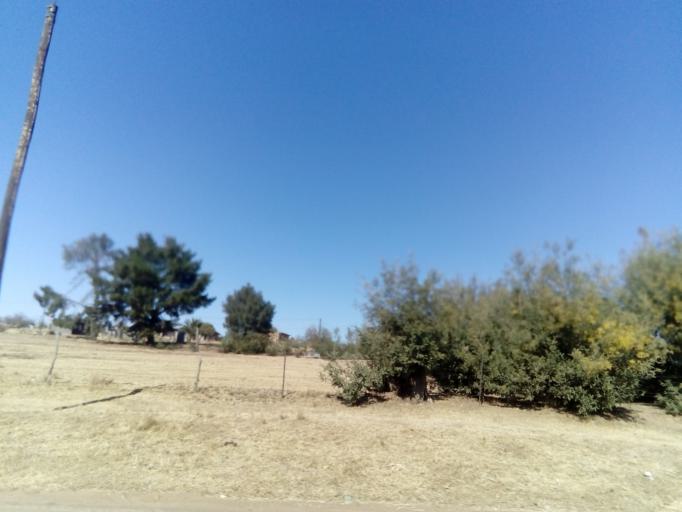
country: LS
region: Berea
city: Teyateyaneng
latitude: -29.1348
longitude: 27.8527
